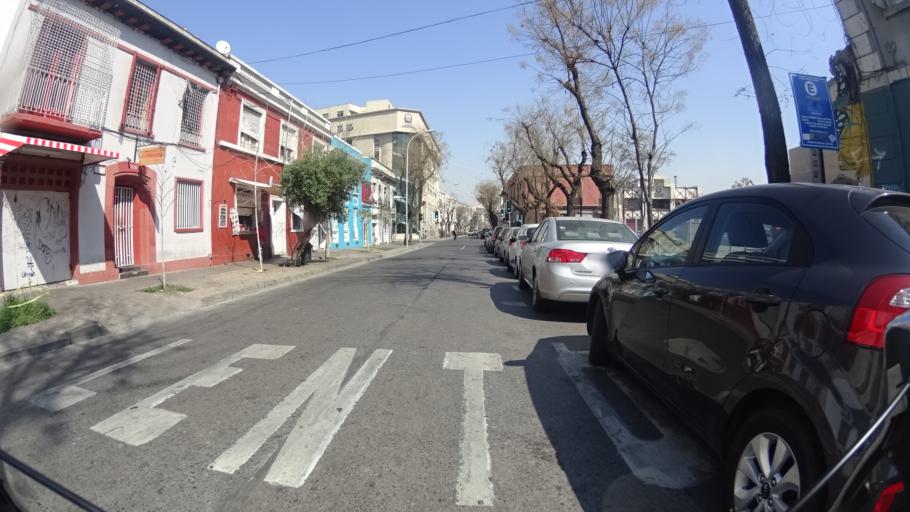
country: CL
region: Santiago Metropolitan
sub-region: Provincia de Santiago
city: Santiago
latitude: -33.4506
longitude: -70.6657
